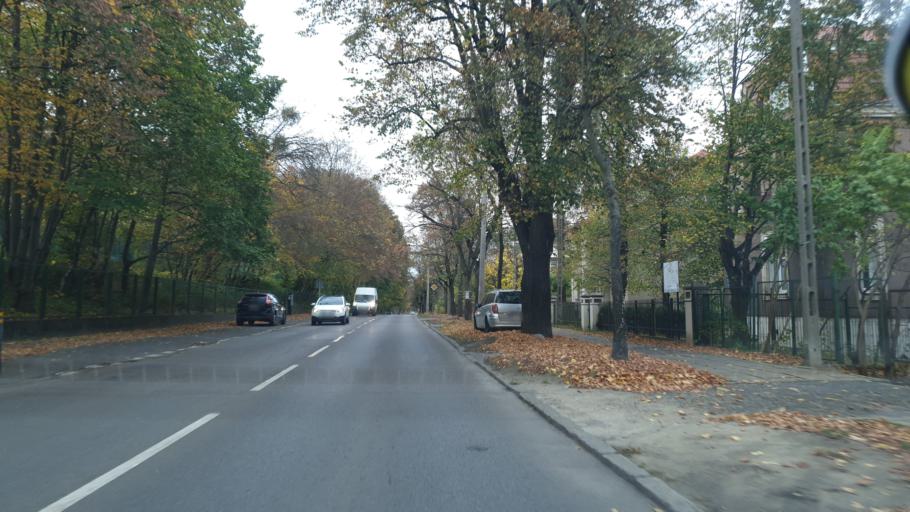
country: PL
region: Pomeranian Voivodeship
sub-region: Sopot
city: Sopot
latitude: 54.3995
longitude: 18.5631
